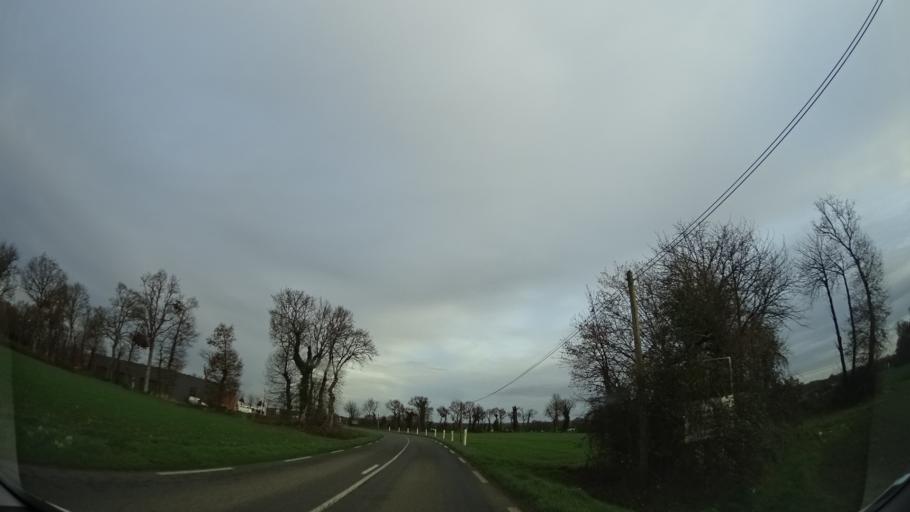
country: FR
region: Brittany
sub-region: Departement des Cotes-d'Armor
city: Evran
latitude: 48.3693
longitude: -1.9702
